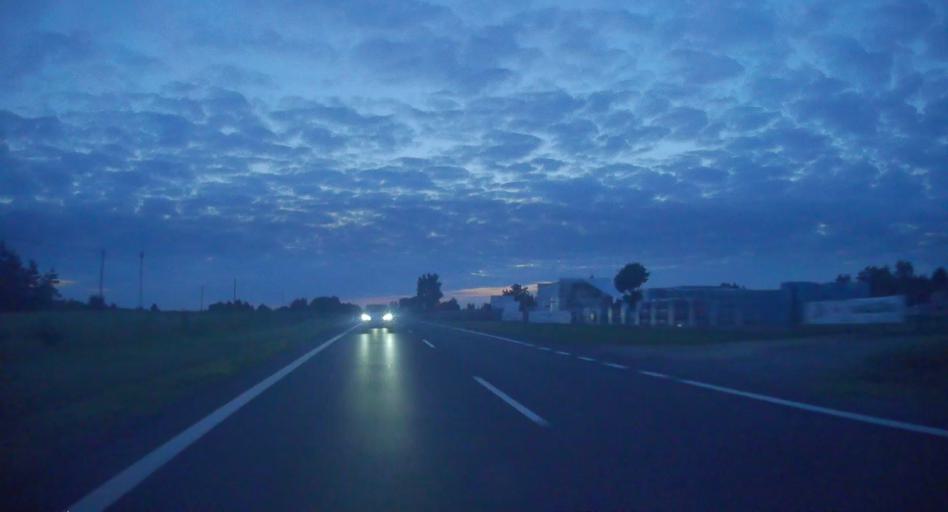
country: PL
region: Silesian Voivodeship
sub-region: Powiat klobucki
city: Klobuck
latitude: 50.8945
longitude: 18.9554
